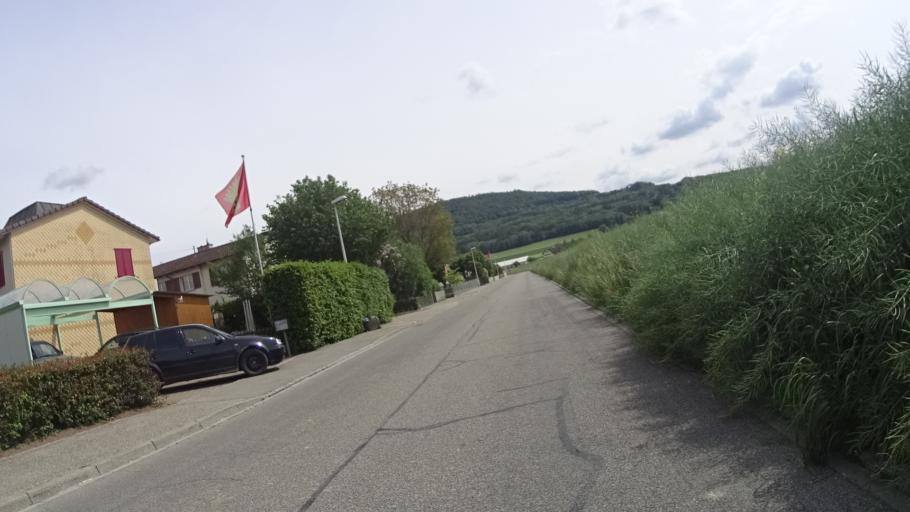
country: CH
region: Aargau
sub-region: Bezirk Rheinfelden
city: Mohlin
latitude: 47.5531
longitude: 7.8425
